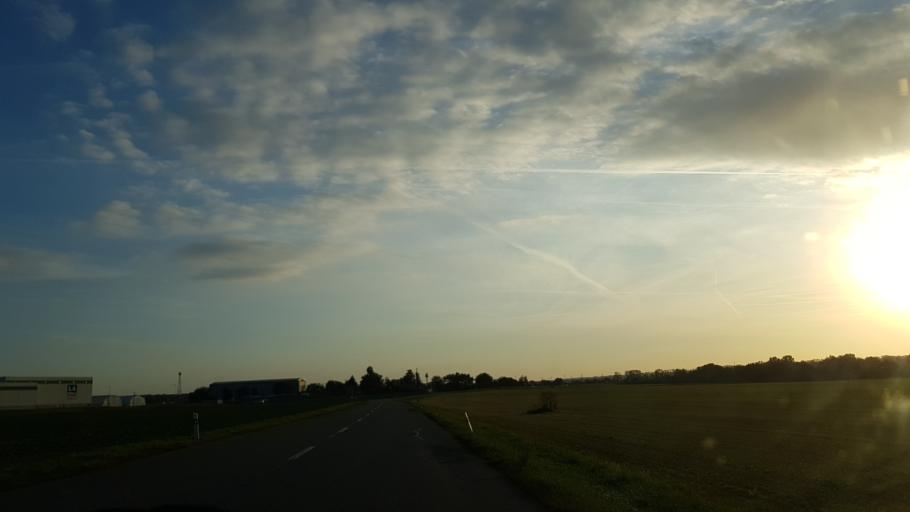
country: CZ
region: Zlin
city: Nedakonice
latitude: 49.0450
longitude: 17.3945
